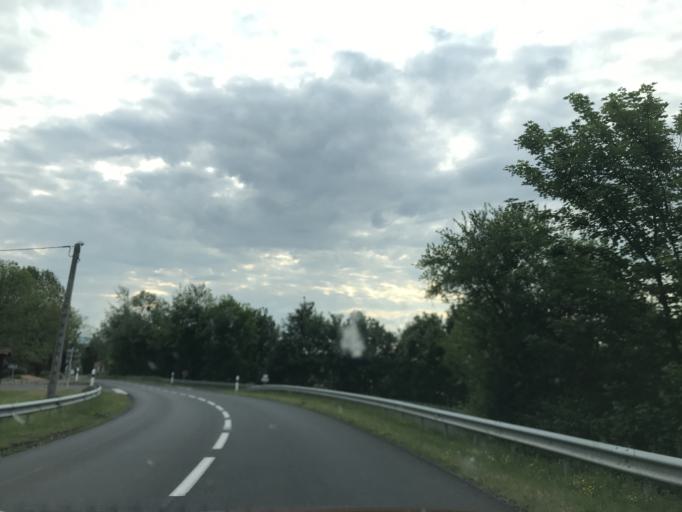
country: FR
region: Auvergne
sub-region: Departement du Puy-de-Dome
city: Maringues
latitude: 45.9155
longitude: 3.3772
